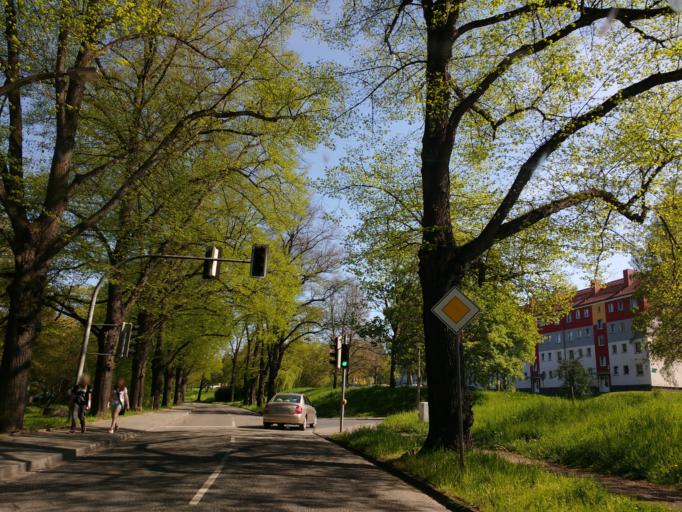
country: DE
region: Saxony-Anhalt
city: Zeitz
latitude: 51.0440
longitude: 12.1312
